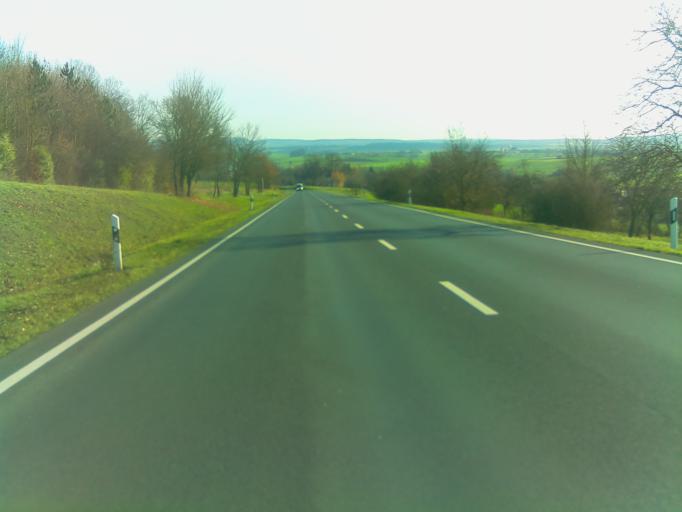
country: DE
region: Bavaria
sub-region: Regierungsbezirk Unterfranken
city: Grosseibstadt
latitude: 50.3044
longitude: 10.3987
